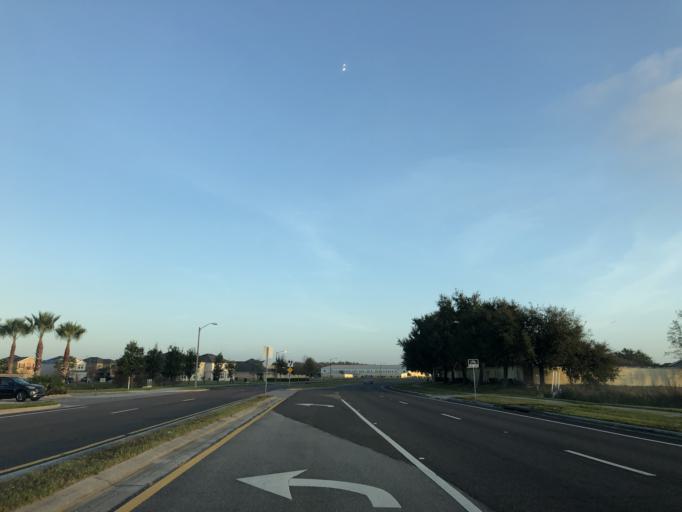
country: US
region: Florida
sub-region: Osceola County
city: Kissimmee
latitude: 28.3276
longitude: -81.4366
